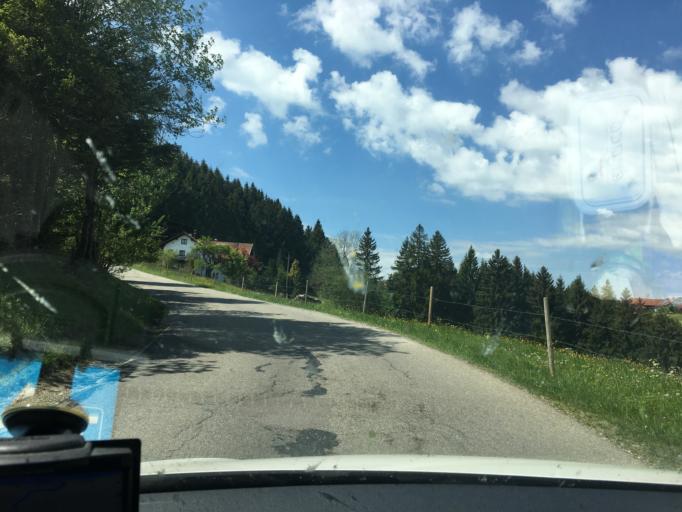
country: DE
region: Bavaria
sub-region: Swabia
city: Wiggensbach
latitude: 47.7406
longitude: 10.2073
